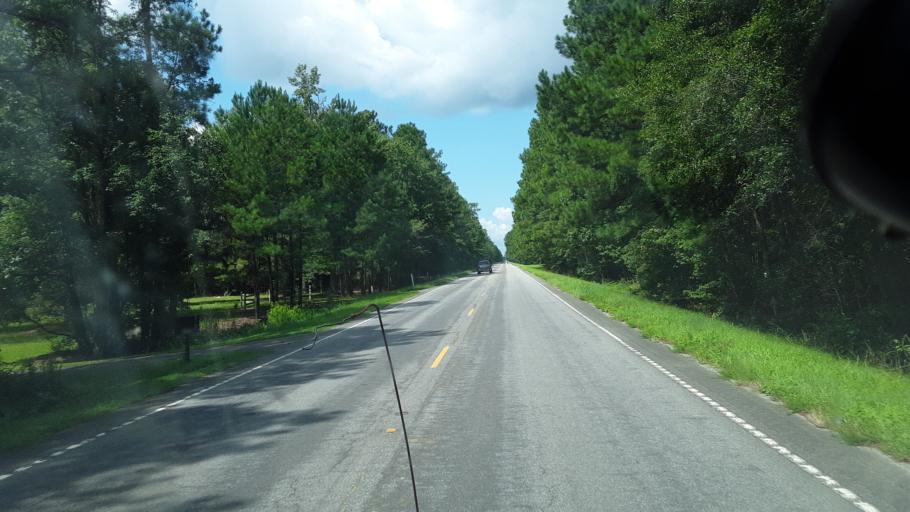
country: US
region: South Carolina
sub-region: Berkeley County
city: Saint Stephen
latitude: 33.2883
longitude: -79.8249
